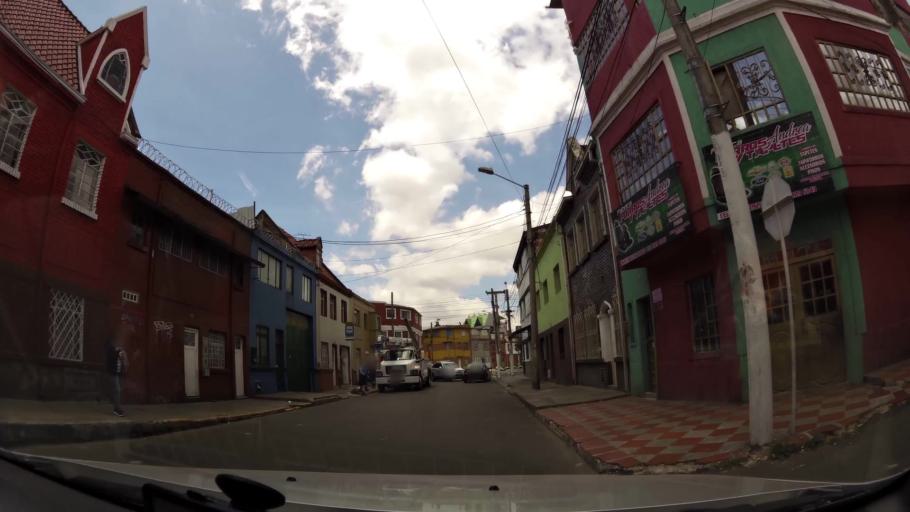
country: CO
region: Bogota D.C.
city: Bogota
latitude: 4.5966
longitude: -74.0897
